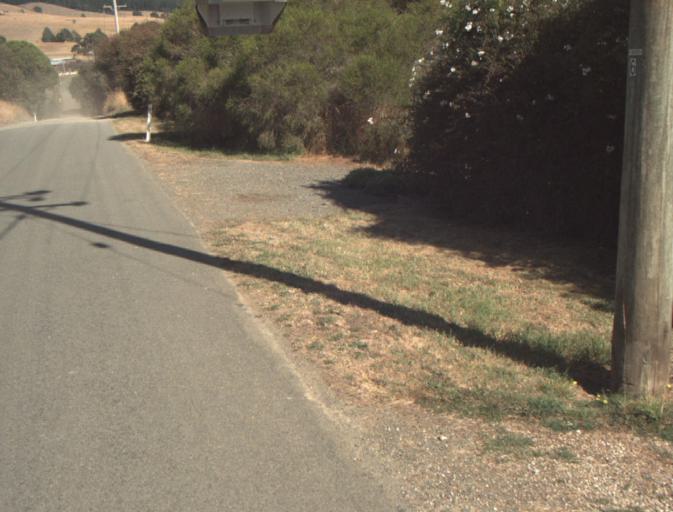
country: AU
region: Tasmania
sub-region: Launceston
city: Mayfield
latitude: -41.1785
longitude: 147.2198
